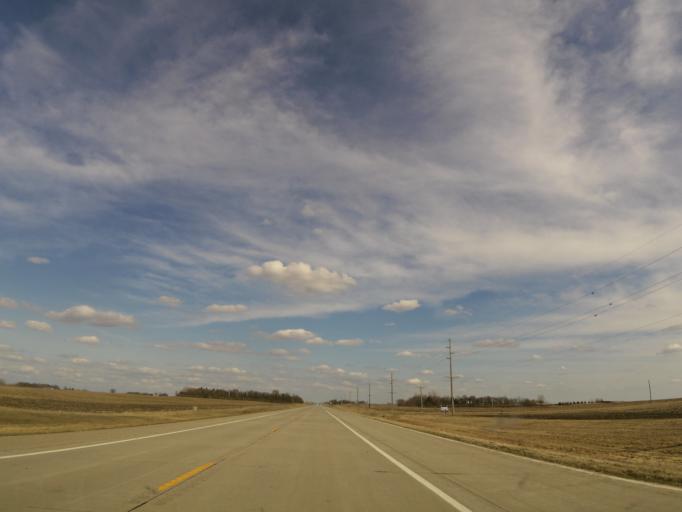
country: US
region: Minnesota
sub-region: Lac qui Parle County
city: Madison
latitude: 44.9358
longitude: -96.1571
